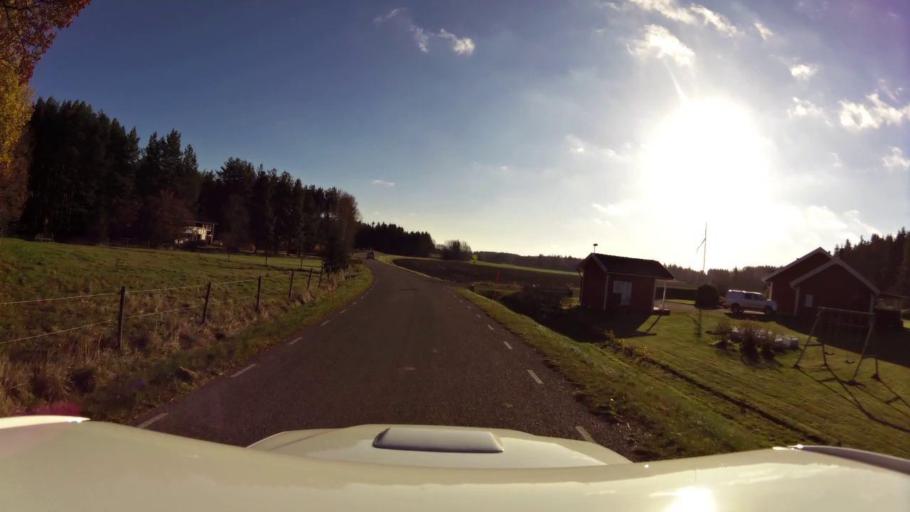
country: SE
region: OEstergoetland
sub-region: Linkopings Kommun
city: Linghem
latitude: 58.4697
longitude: 15.7642
